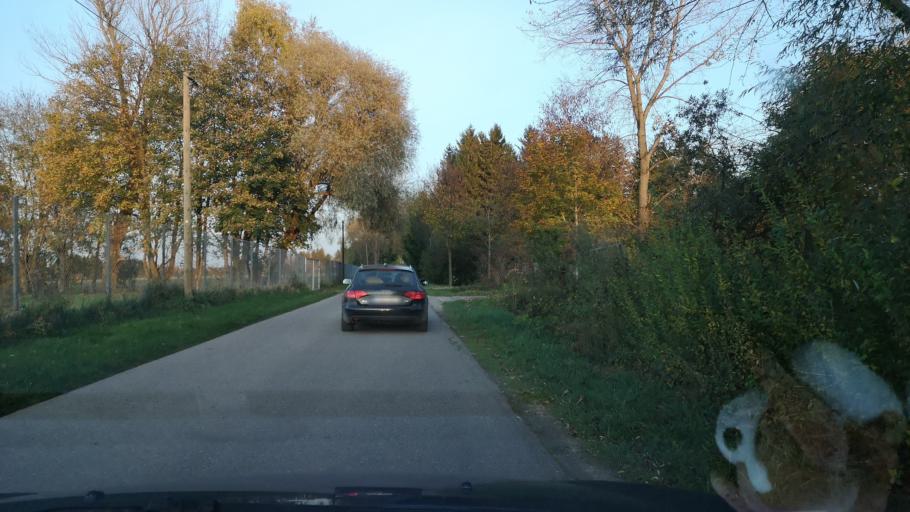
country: DE
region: Bavaria
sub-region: Upper Bavaria
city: Eichenried
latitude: 48.2464
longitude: 11.7473
